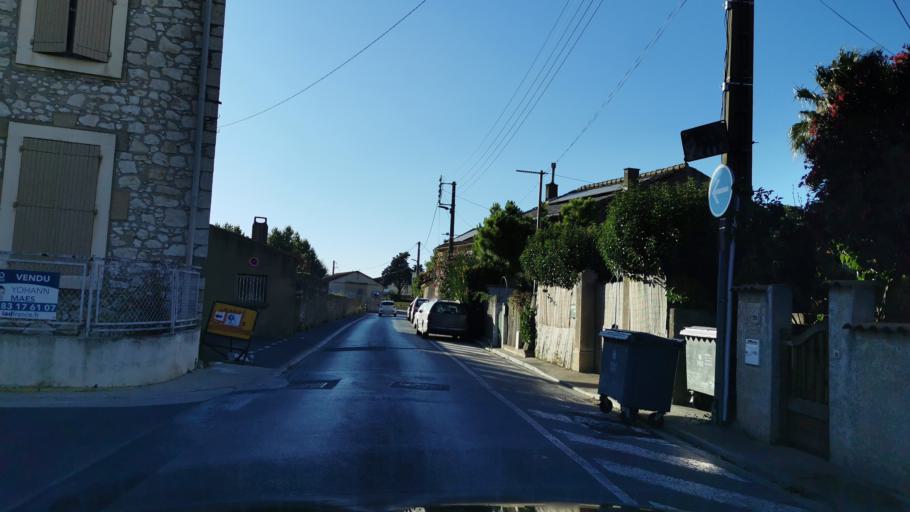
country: FR
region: Languedoc-Roussillon
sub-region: Departement de l'Aude
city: Ouveillan
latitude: 43.2459
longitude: 3.0016
